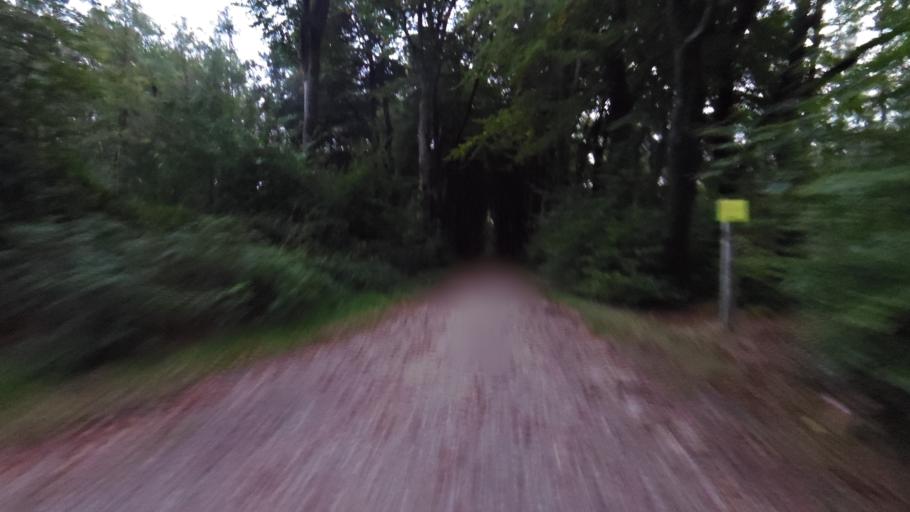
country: NL
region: Gelderland
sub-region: Gemeente Renkum
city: Doorwerth
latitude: 51.9871
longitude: 5.8127
